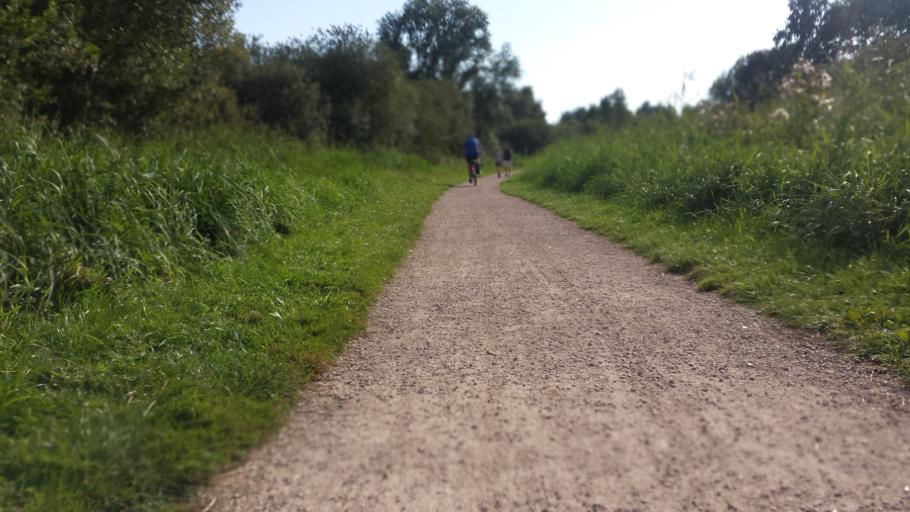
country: GB
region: England
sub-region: Cambridgeshire
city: Soham
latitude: 52.3088
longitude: 0.2901
